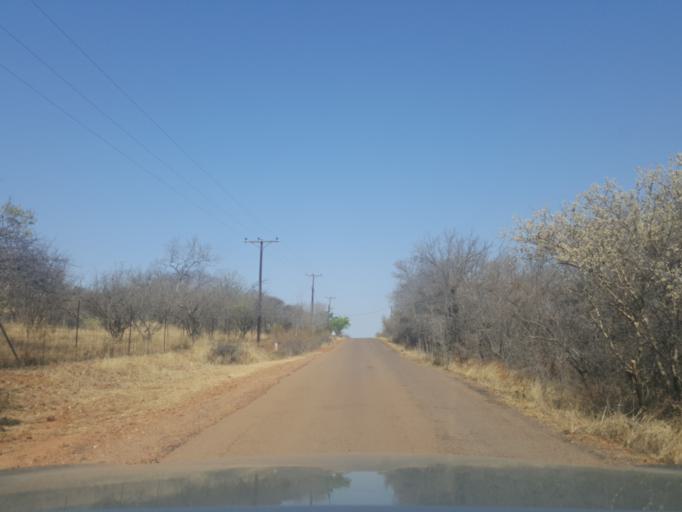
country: BW
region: Kweneng
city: Gabane
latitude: -24.7395
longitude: 25.8169
